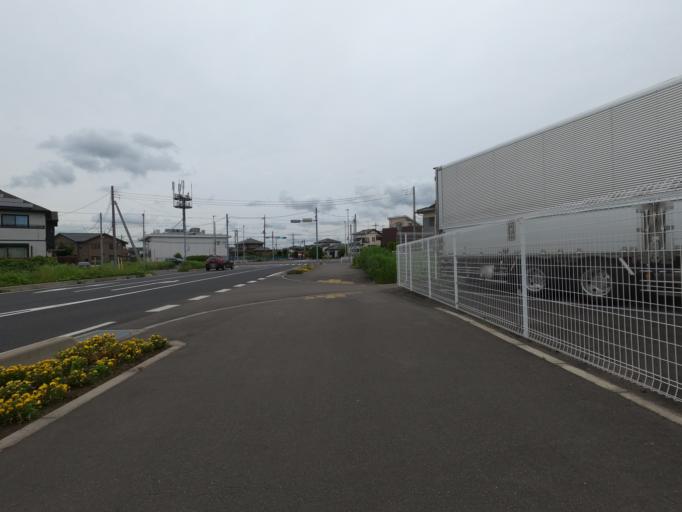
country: JP
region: Ibaraki
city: Moriya
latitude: 35.9505
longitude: 139.9825
